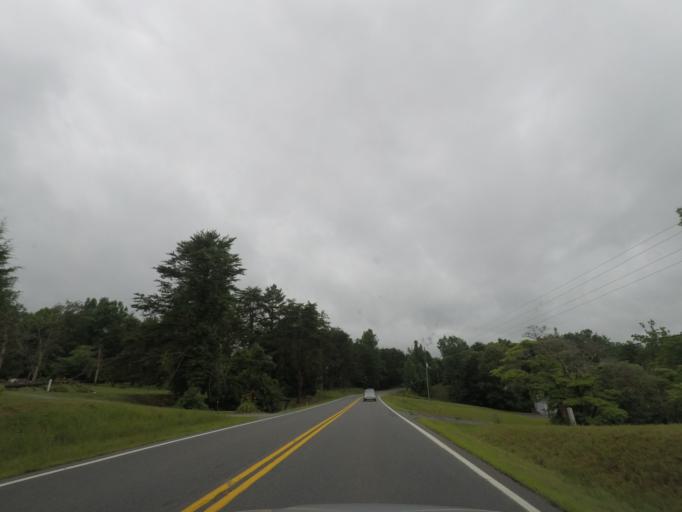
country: US
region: Virginia
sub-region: Fluvanna County
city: Palmyra
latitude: 37.8868
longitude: -78.2629
